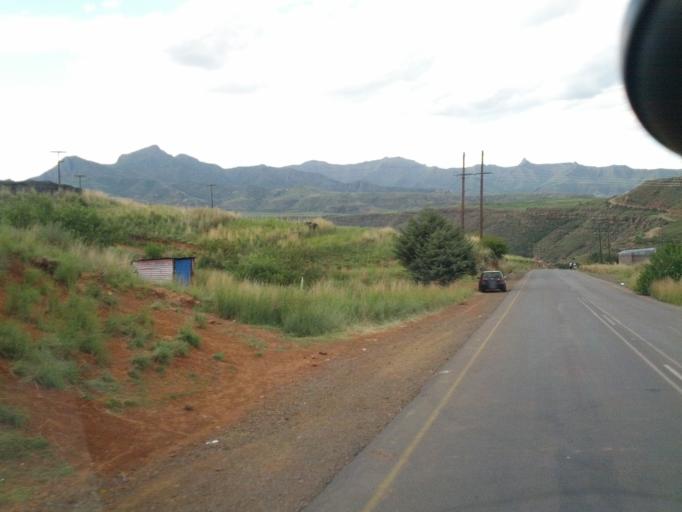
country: LS
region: Qacha's Nek
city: Qacha's Nek
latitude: -30.0754
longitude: 28.6223
